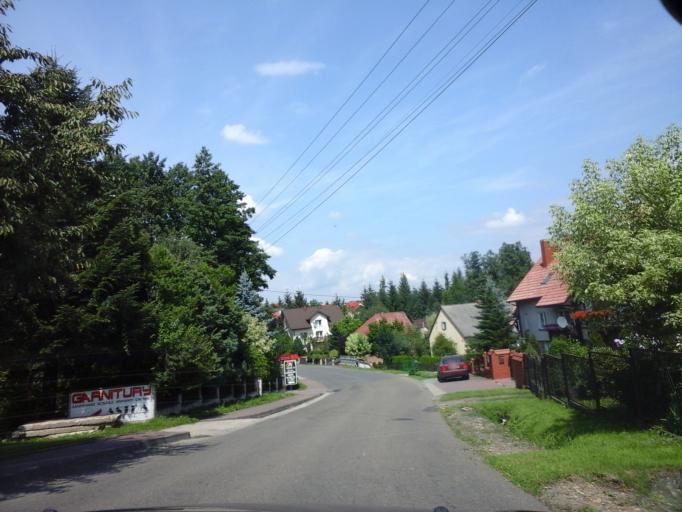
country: PL
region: Lesser Poland Voivodeship
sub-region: Powiat wadowicki
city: Bachowice
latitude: 49.9698
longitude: 19.4966
